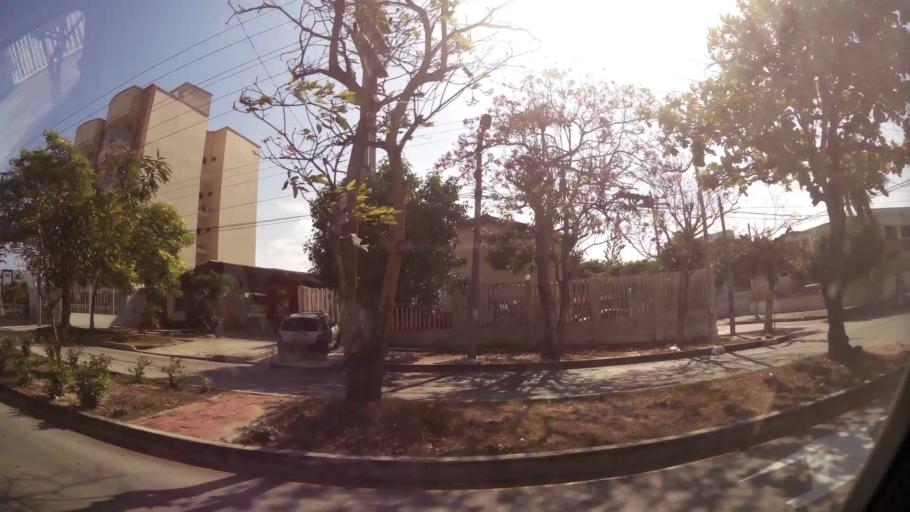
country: CO
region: Atlantico
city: Barranquilla
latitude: 10.9914
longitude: -74.8226
